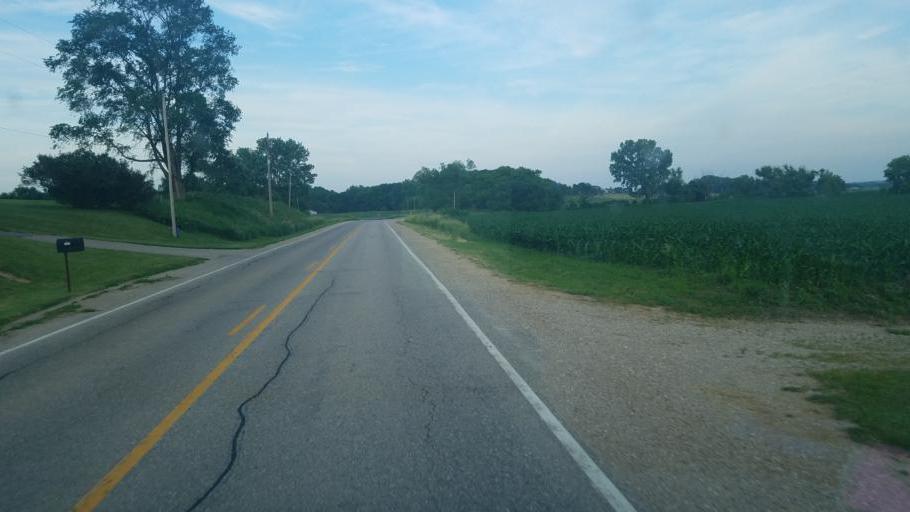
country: US
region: Iowa
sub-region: Tama County
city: Tama
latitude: 41.9592
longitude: -92.4305
